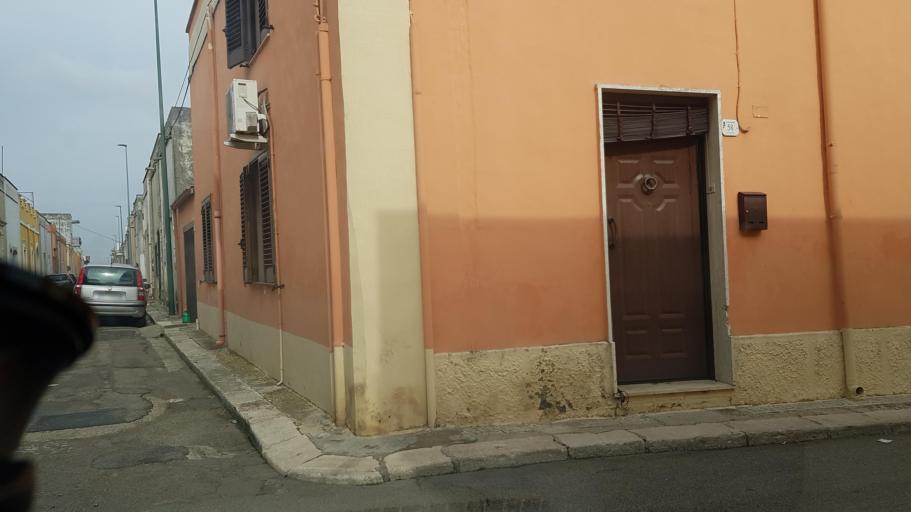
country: IT
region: Apulia
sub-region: Provincia di Lecce
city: Guagnano
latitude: 40.4018
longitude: 17.9473
